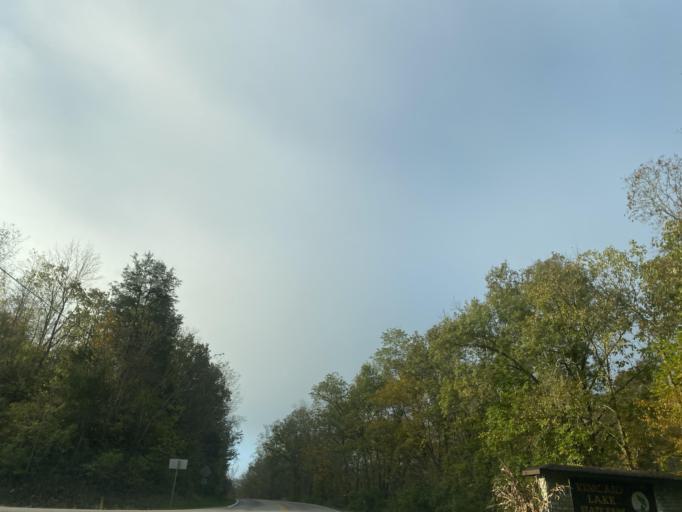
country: US
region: Kentucky
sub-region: Pendleton County
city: Falmouth
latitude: 38.7198
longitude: -84.3004
